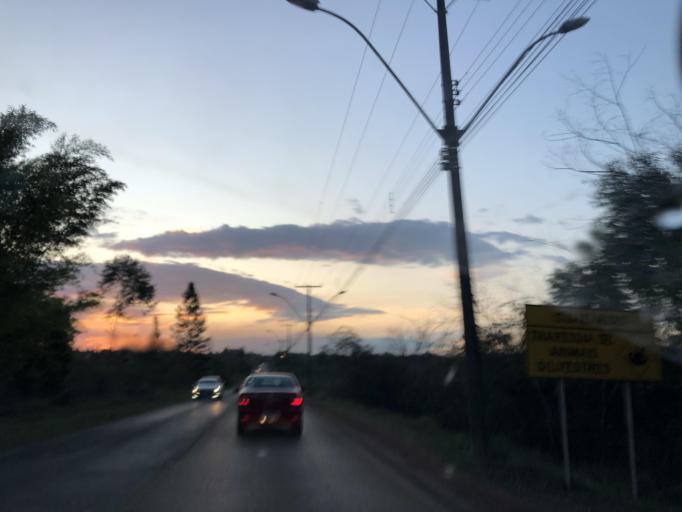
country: BR
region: Federal District
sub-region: Brasilia
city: Brasilia
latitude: -15.8956
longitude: -47.9394
